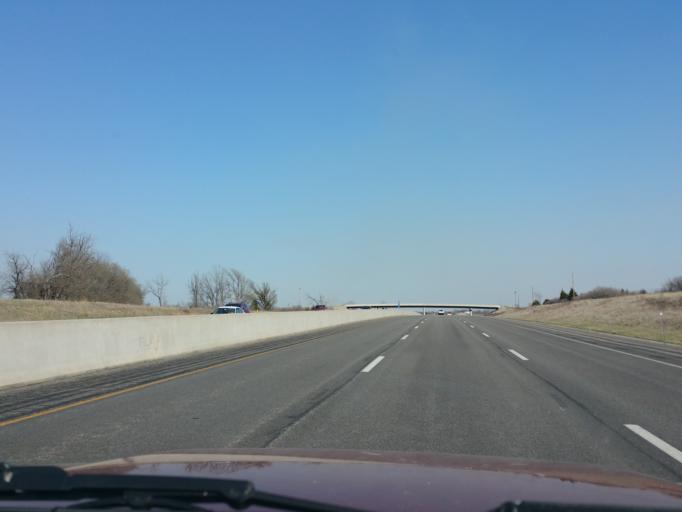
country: US
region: Kansas
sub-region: Douglas County
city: Lawrence
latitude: 39.0075
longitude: -95.4518
